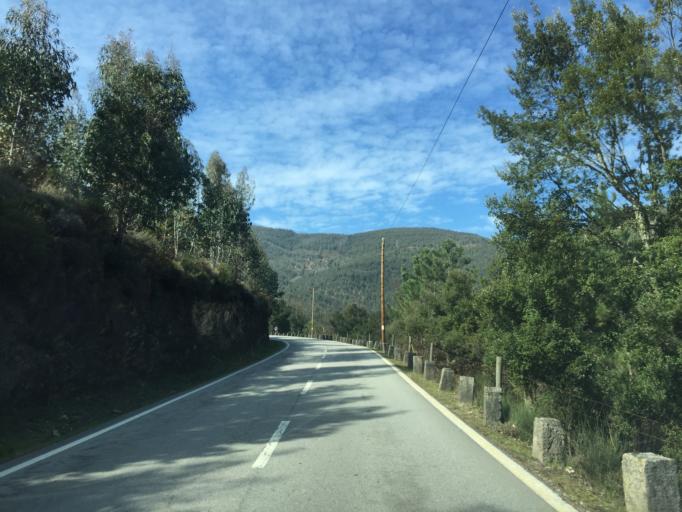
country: PT
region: Aveiro
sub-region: Arouca
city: Arouca
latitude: 40.9565
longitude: -8.1765
